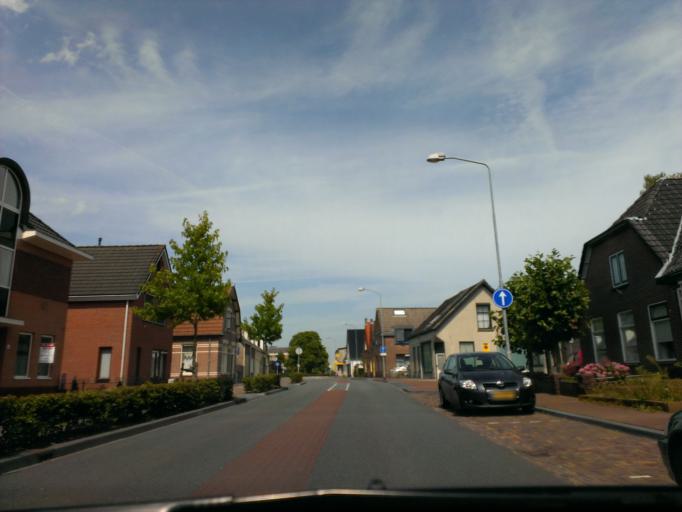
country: NL
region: Gelderland
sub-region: Gemeente Hattem
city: Hattem
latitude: 52.4723
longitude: 6.0712
